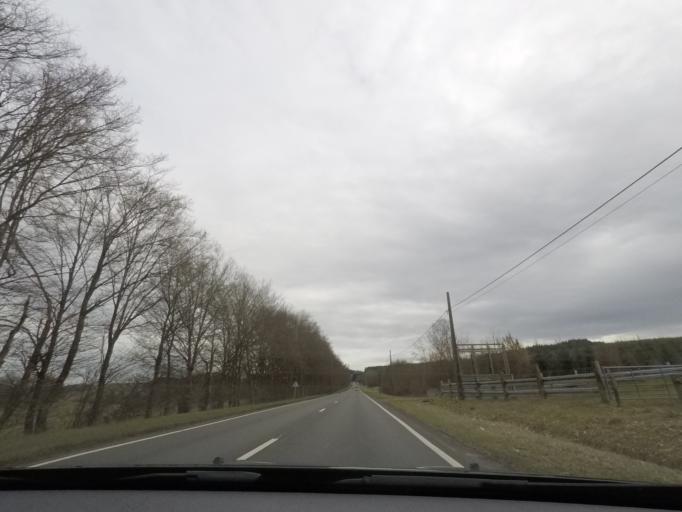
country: BE
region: Wallonia
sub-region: Province du Luxembourg
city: Bastogne
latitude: 49.9792
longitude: 5.7692
